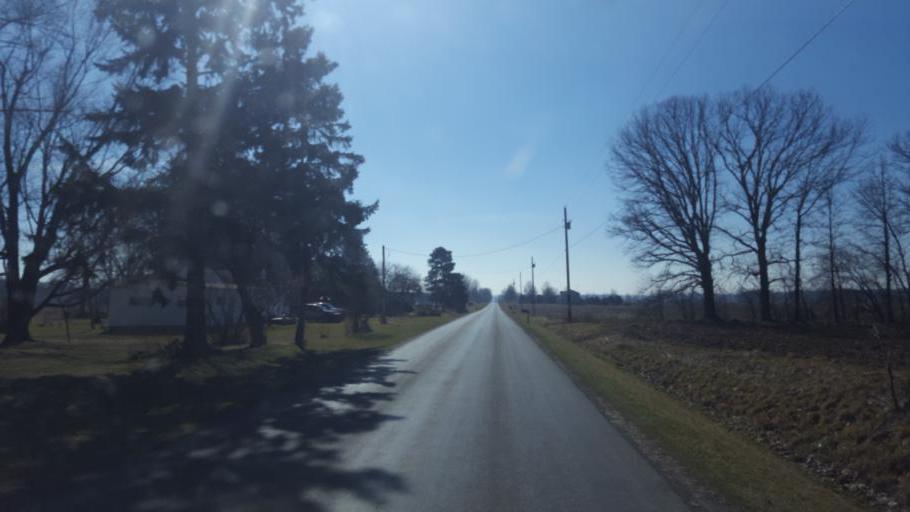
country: US
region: Ohio
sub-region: Huron County
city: Greenwich
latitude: 41.0272
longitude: -82.5841
